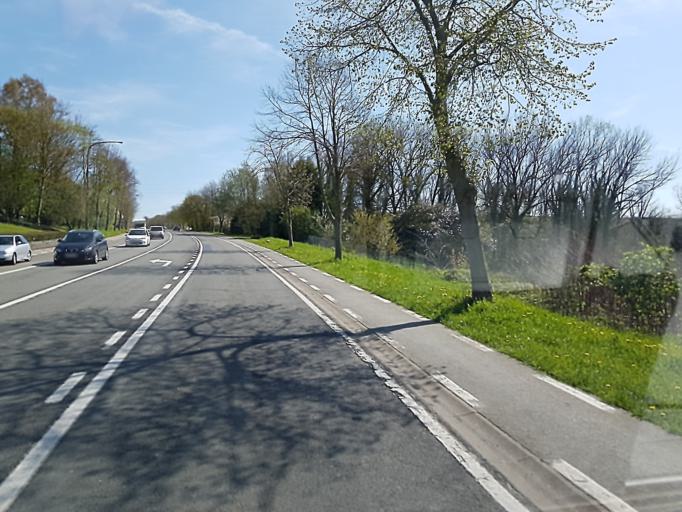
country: BE
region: Flanders
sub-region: Provincie West-Vlaanderen
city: Anzegem
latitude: 50.7766
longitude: 3.5211
